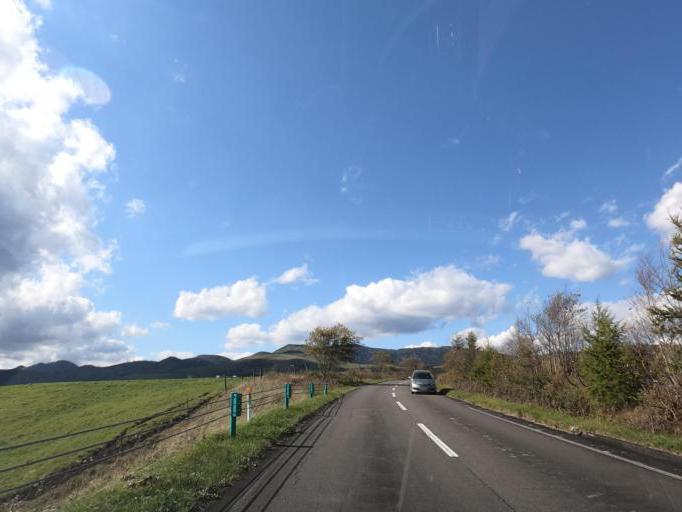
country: JP
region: Hokkaido
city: Otofuke
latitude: 43.2795
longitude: 143.2232
